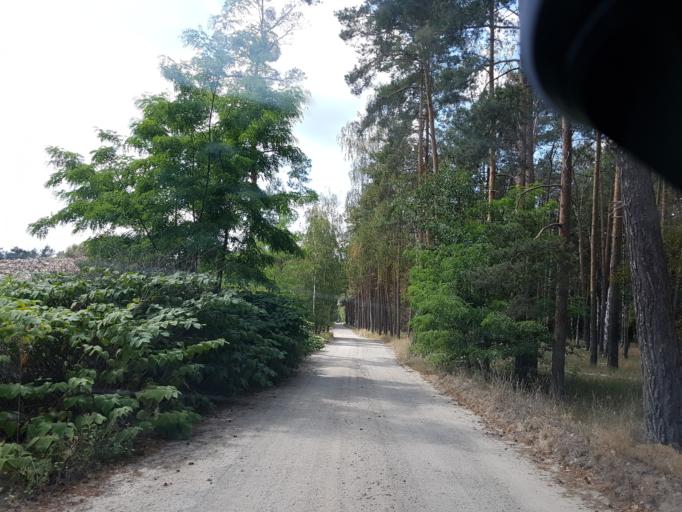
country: DE
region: Brandenburg
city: Heinersbruck
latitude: 51.7130
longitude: 14.4468
